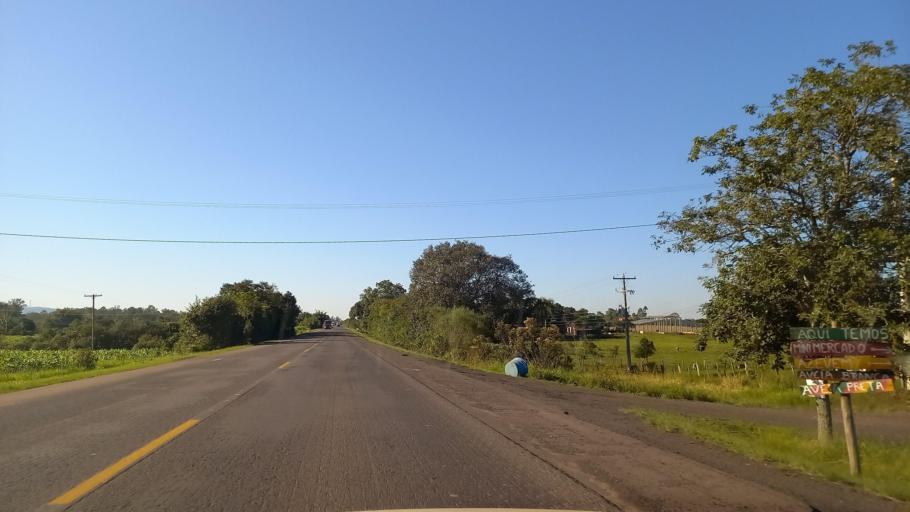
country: BR
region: Rio Grande do Sul
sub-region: Venancio Aires
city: Venancio Aires
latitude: -29.6726
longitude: -52.0202
